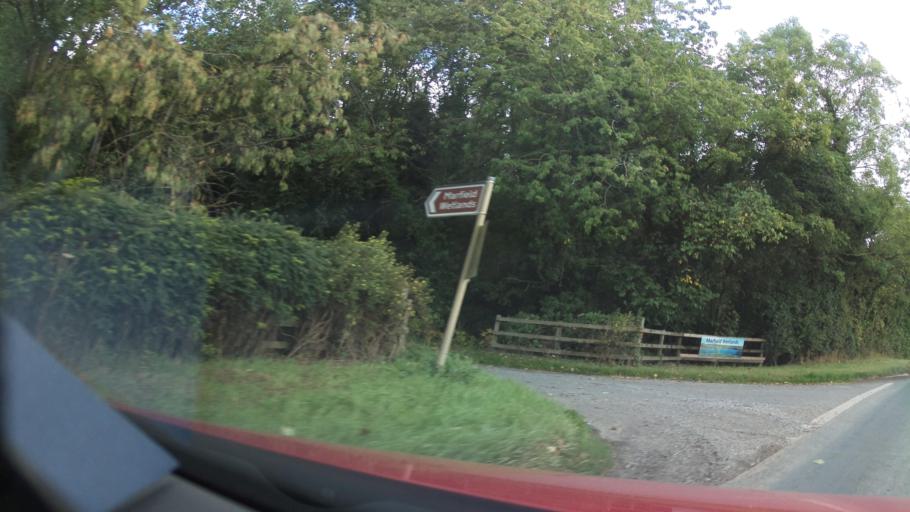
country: GB
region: England
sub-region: North Yorkshire
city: Bedale
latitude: 54.2310
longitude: -1.6665
